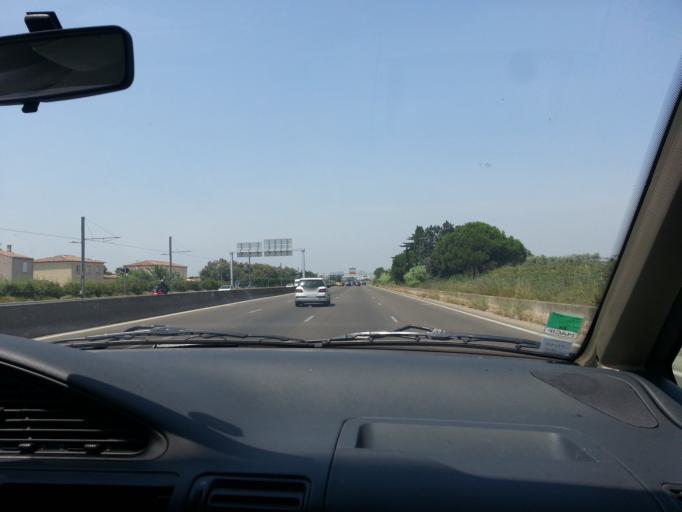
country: FR
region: Languedoc-Roussillon
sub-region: Departement de l'Herault
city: Perols
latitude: 43.5589
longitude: 3.9633
